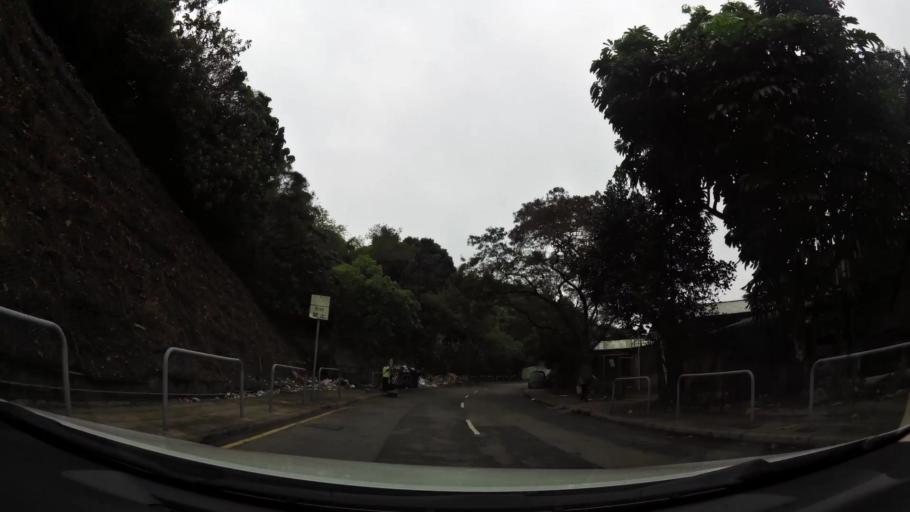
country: HK
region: Wanchai
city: Wan Chai
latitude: 22.2396
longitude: 114.1661
